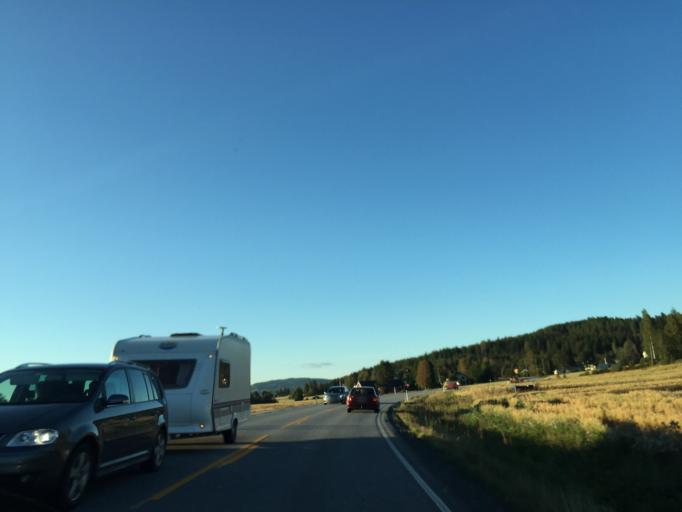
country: NO
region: Hedmark
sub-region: Nord-Odal
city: Sand
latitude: 60.4069
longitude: 11.5189
